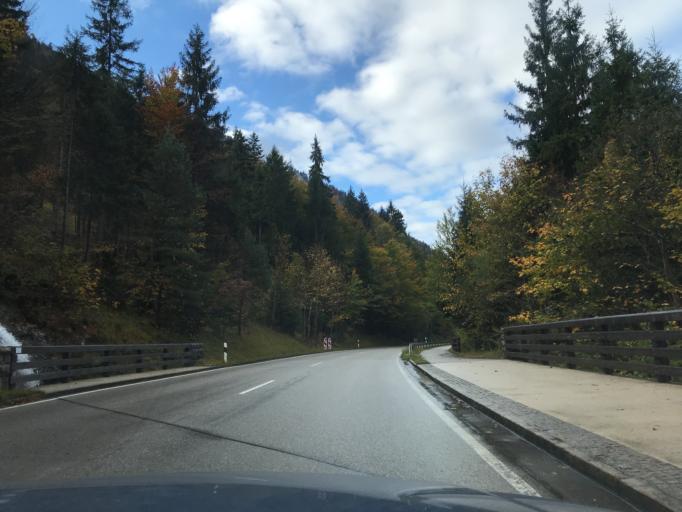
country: DE
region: Bavaria
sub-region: Upper Bavaria
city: Lenggries
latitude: 47.6065
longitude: 11.5819
